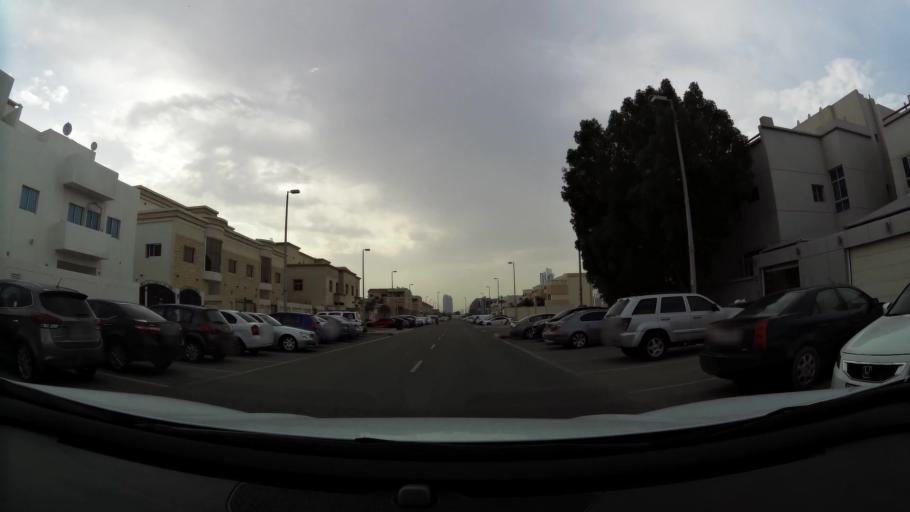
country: AE
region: Abu Dhabi
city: Abu Dhabi
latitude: 24.4745
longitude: 54.3831
